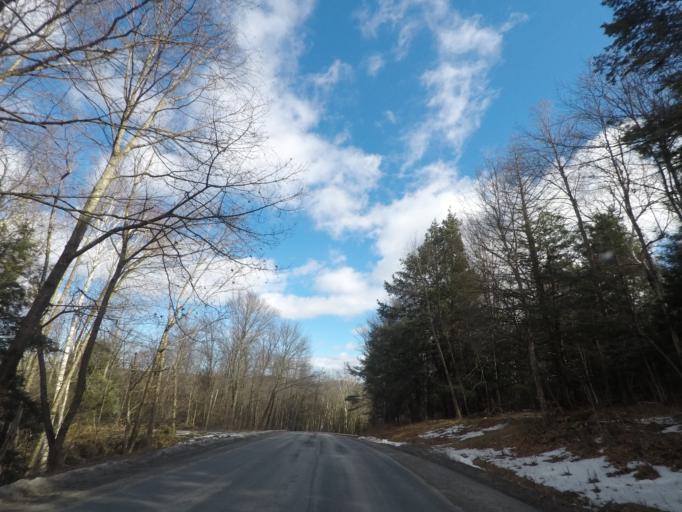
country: US
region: New York
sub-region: Rensselaer County
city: Averill Park
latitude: 42.6678
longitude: -73.5091
